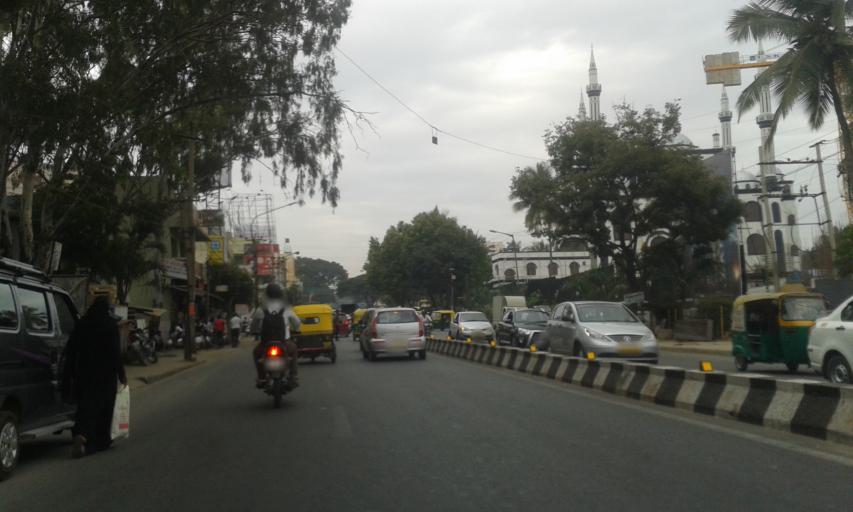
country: IN
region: Karnataka
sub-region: Bangalore Urban
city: Bangalore
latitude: 12.9223
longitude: 77.6003
